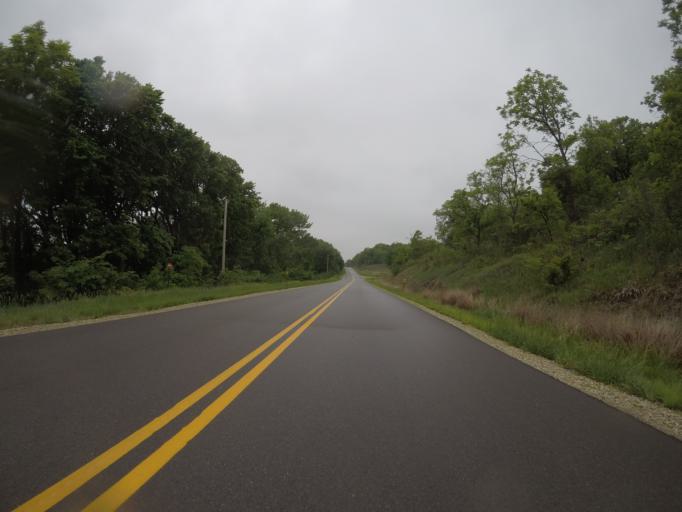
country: US
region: Kansas
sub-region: Pottawatomie County
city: Wamego
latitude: 39.1833
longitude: -96.3559
